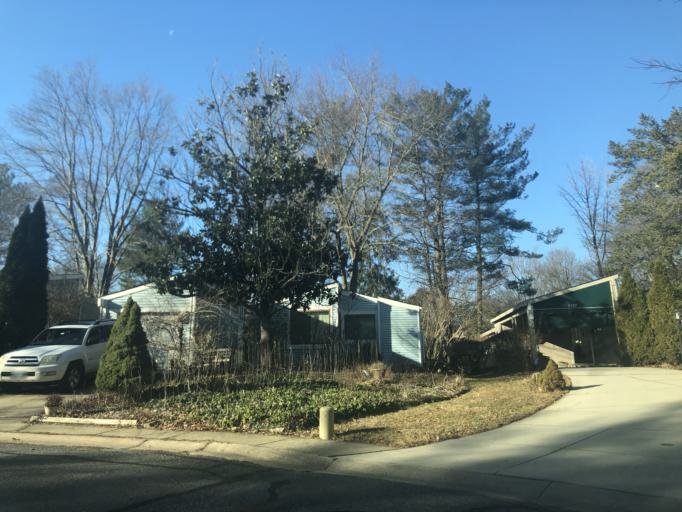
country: US
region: Maryland
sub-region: Howard County
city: Columbia
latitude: 39.2026
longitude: -76.8435
